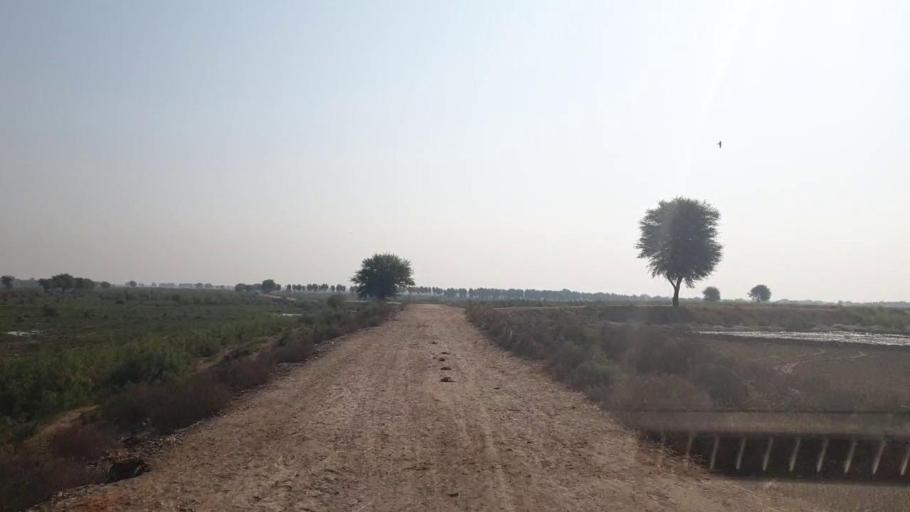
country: PK
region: Sindh
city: Sehwan
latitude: 26.4515
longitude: 67.8319
